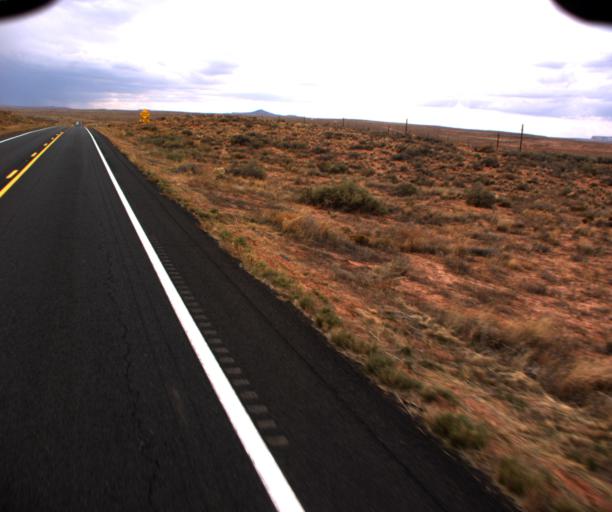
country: US
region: Arizona
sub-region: Coconino County
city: Kaibito
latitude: 36.3960
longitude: -110.8678
